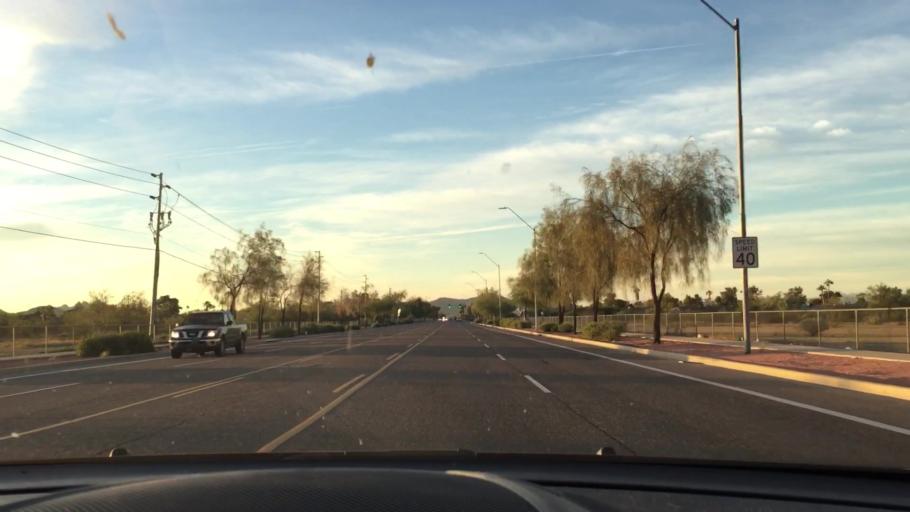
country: US
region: Arizona
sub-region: Maricopa County
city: Glendale
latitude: 33.6795
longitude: -112.0829
